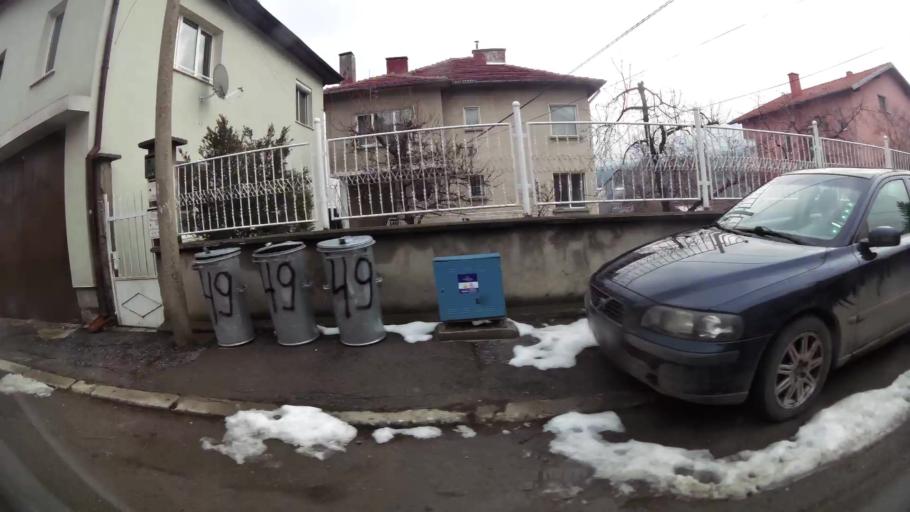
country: BG
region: Sofia-Capital
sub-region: Stolichna Obshtina
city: Sofia
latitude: 42.6619
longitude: 23.2414
